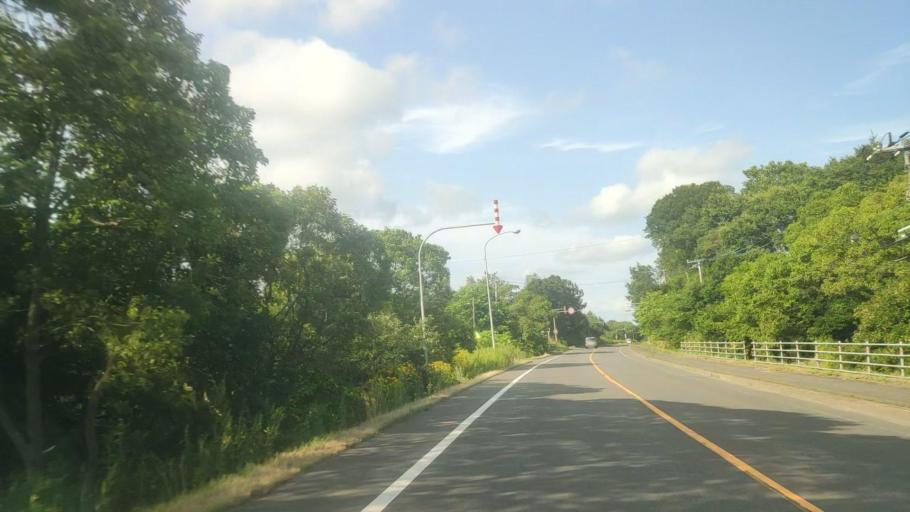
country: JP
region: Hokkaido
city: Chitose
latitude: 42.7341
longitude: 141.7765
